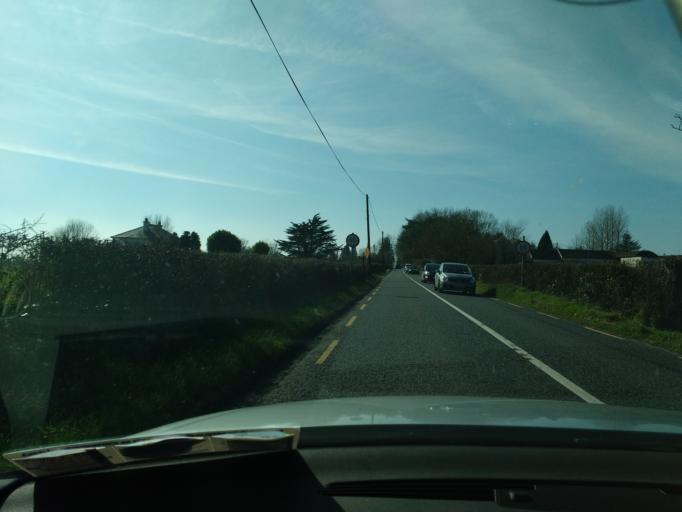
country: IE
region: Munster
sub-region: County Limerick
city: Castleconnell
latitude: 52.6952
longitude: -8.4668
